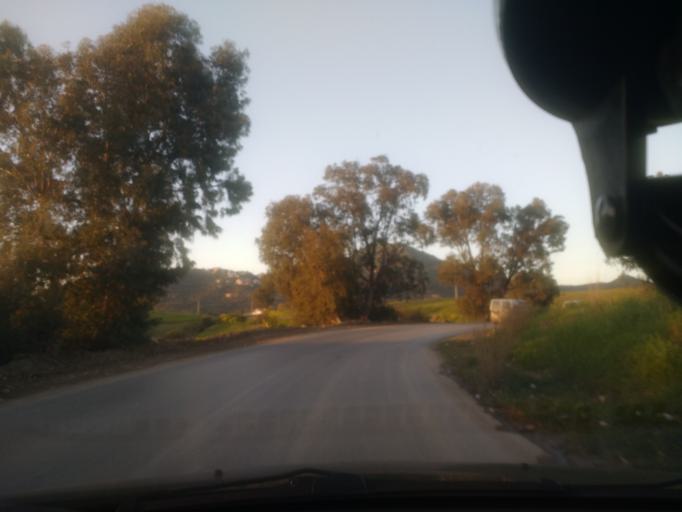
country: DZ
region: Boumerdes
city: Makouda
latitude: 36.7673
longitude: 4.0653
